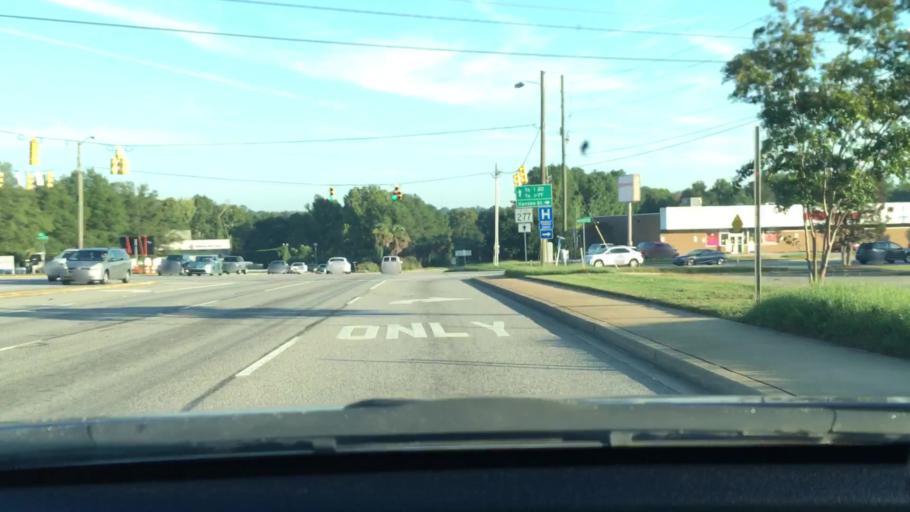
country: US
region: South Carolina
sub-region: Richland County
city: Columbia
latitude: 34.0236
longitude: -81.0377
